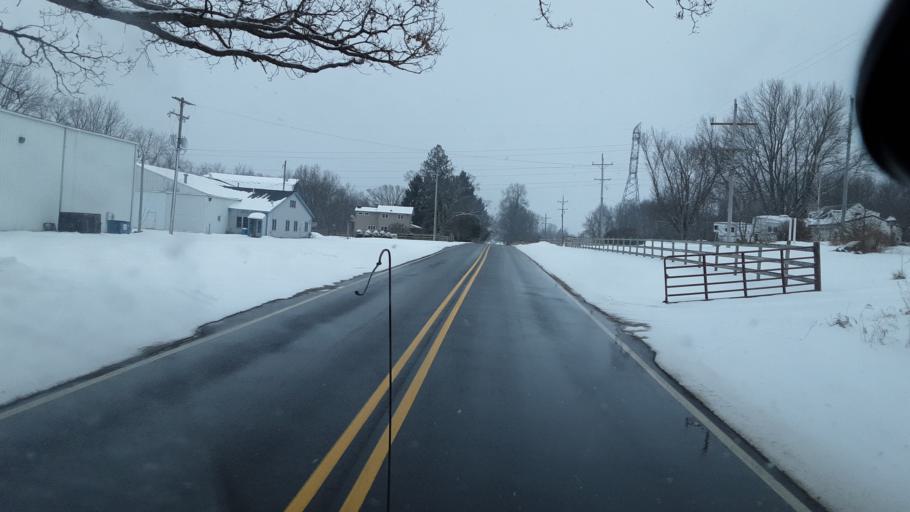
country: US
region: Michigan
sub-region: Ingham County
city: Leslie
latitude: 42.4181
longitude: -84.4433
